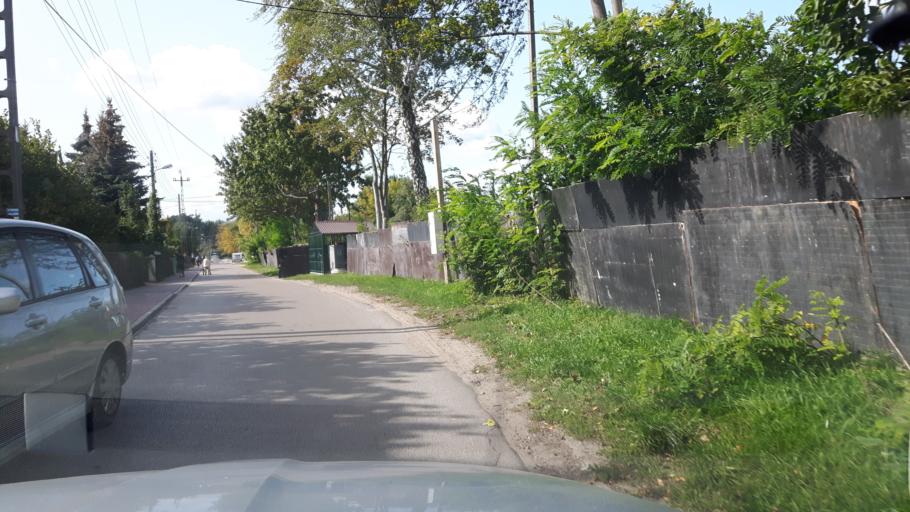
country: PL
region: Masovian Voivodeship
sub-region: Powiat legionowski
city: Nieporet
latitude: 52.4561
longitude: 21.0108
